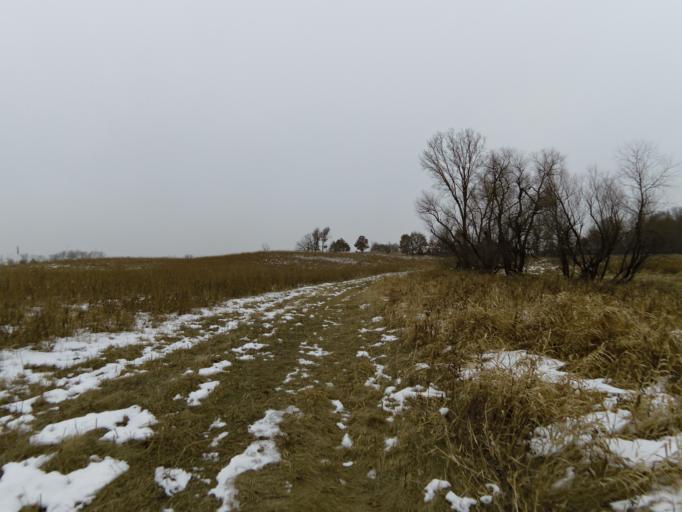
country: US
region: Minnesota
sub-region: Washington County
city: Lake Elmo
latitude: 44.9839
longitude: -92.9119
